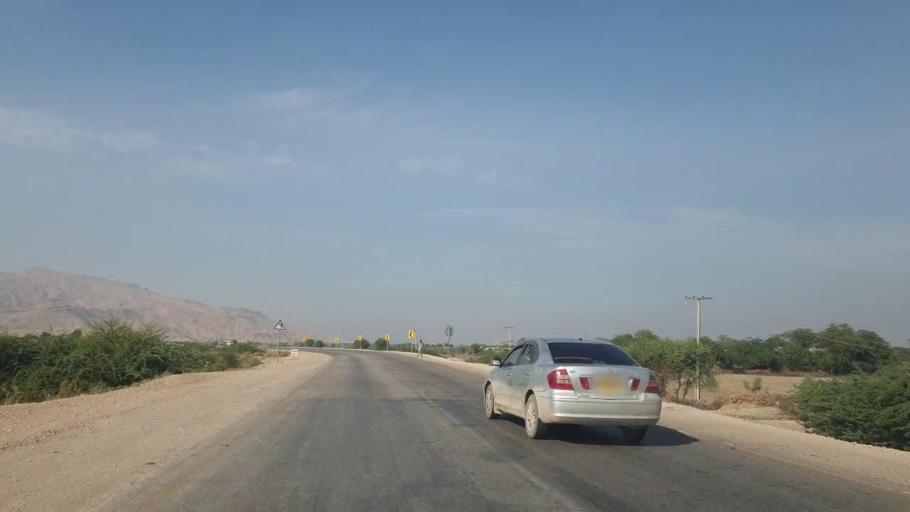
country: PK
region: Sindh
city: Sehwan
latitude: 26.2675
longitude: 67.9038
